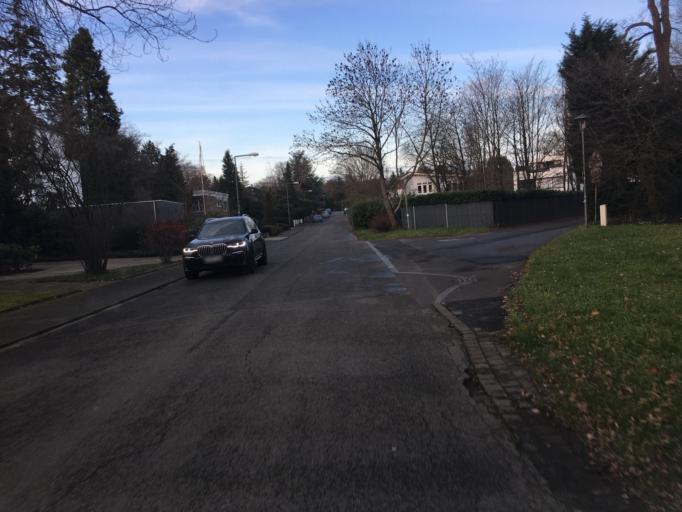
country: DE
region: North Rhine-Westphalia
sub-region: Regierungsbezirk Koln
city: Bayenthal
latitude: 50.8729
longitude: 6.9781
